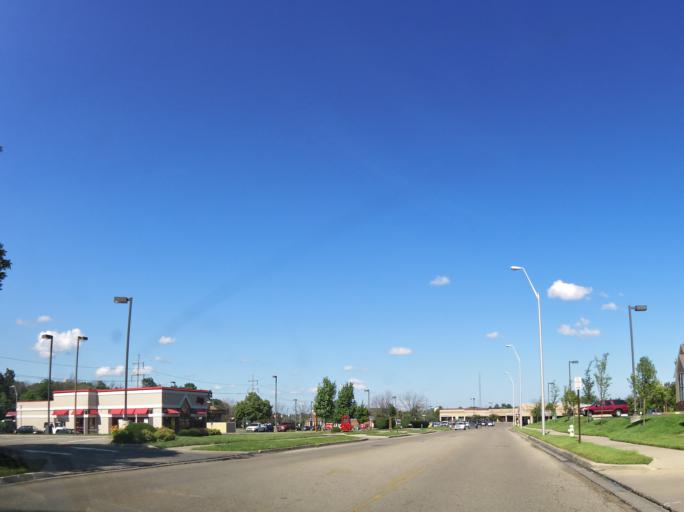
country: US
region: Ohio
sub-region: Greene County
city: Wright-Patterson AFB
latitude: 39.7777
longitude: -84.0571
